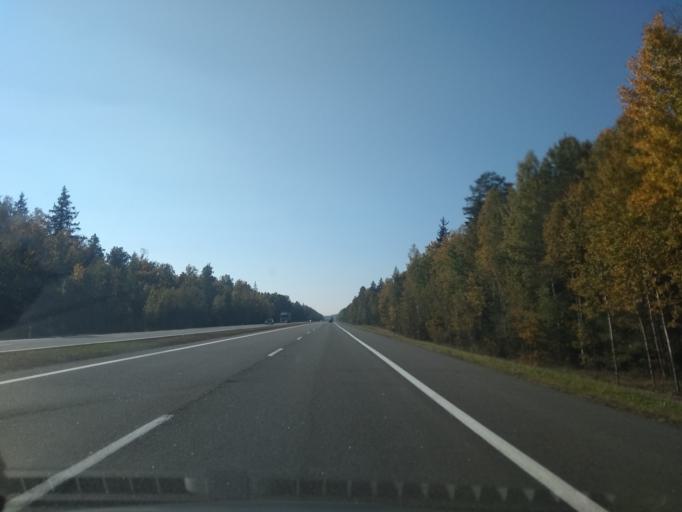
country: BY
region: Brest
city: Ivatsevichy
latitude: 52.8434
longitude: 25.6255
